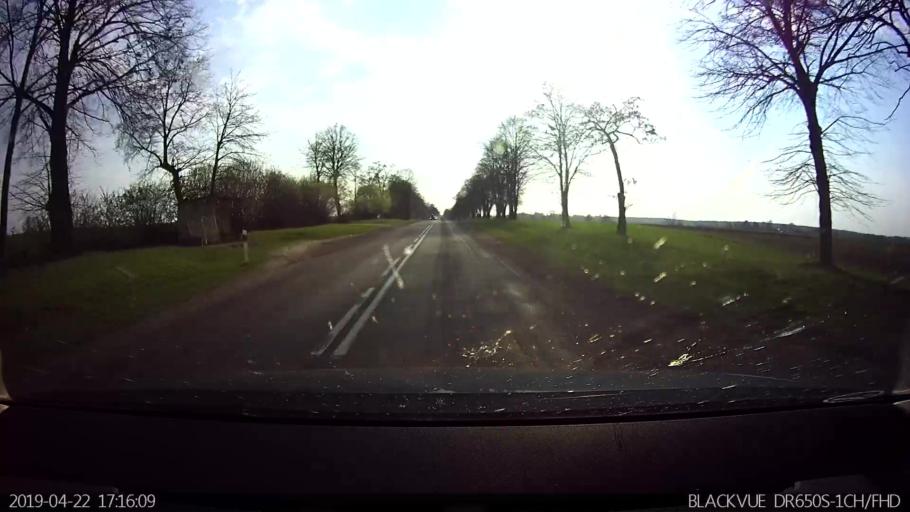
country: PL
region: Masovian Voivodeship
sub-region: Powiat sokolowski
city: Repki
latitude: 52.3963
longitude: 22.4690
